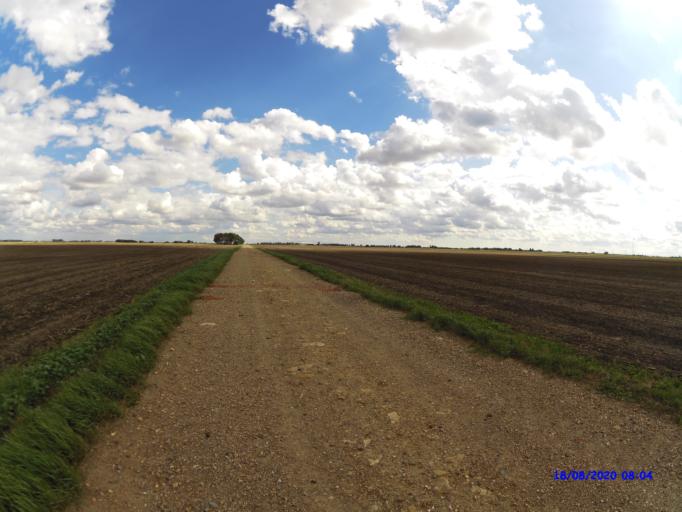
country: GB
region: England
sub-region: Cambridgeshire
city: Whittlesey
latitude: 52.5137
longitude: -0.0852
